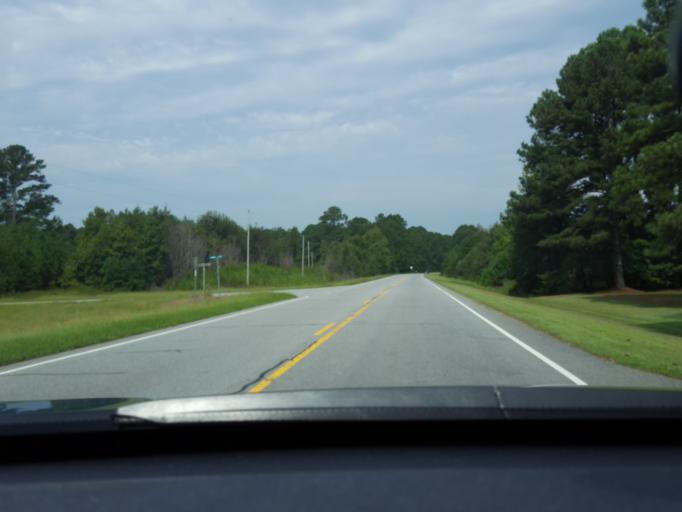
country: US
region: North Carolina
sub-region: Washington County
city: Plymouth
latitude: 35.9705
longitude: -76.7561
